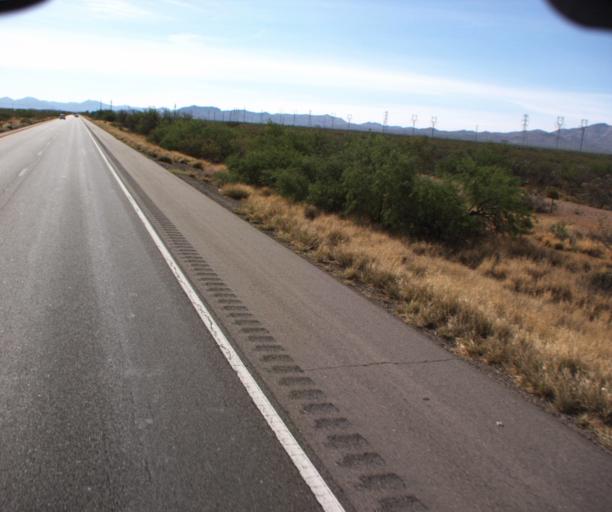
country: US
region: Arizona
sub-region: Pima County
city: Vail
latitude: 32.0414
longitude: -110.7423
